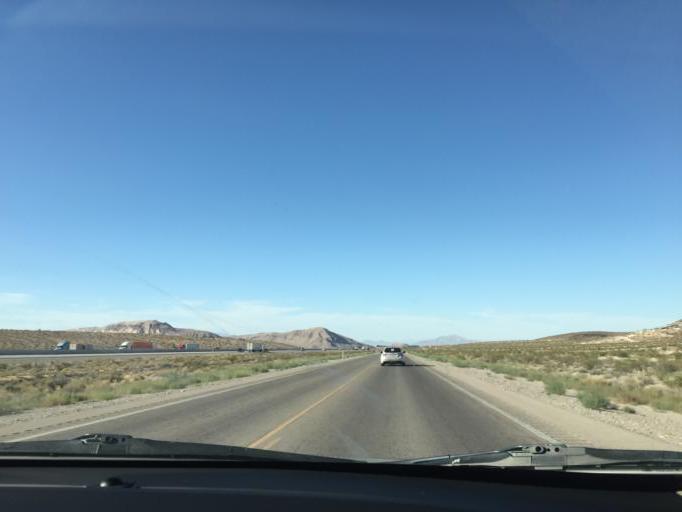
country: US
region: Nevada
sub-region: Clark County
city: Enterprise
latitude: 35.9005
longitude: -115.2129
